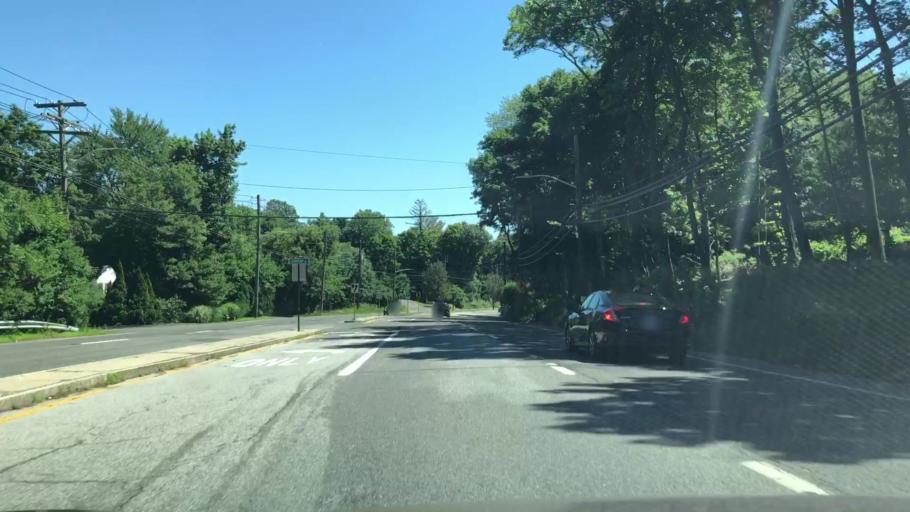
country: US
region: New York
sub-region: Westchester County
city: Scarsdale
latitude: 40.9975
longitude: -73.7467
